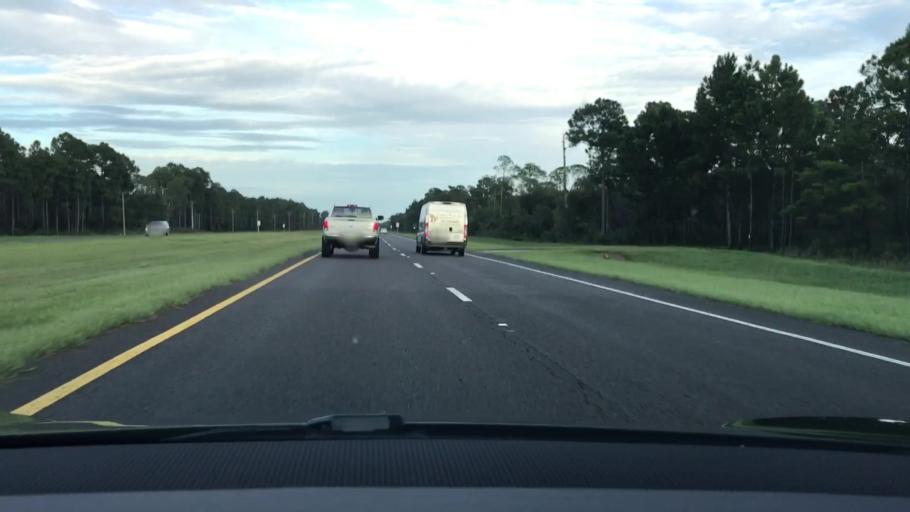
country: US
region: Florida
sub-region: Walton County
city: Seaside
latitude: 30.3624
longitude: -86.1688
